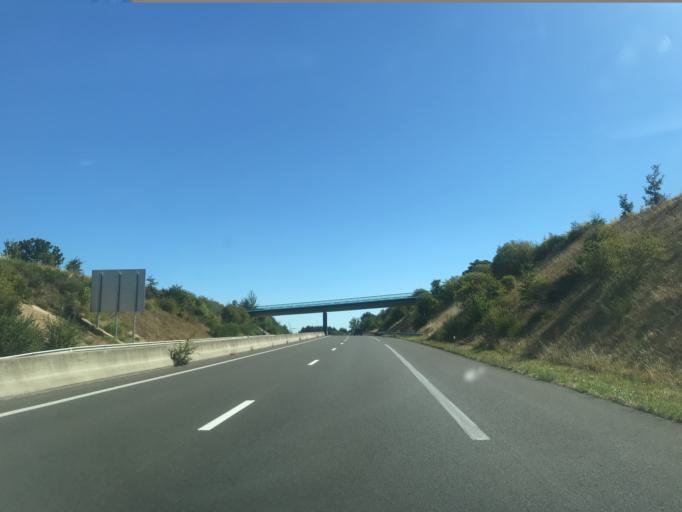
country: FR
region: Auvergne
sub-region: Departement de l'Allier
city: Huriel
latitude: 46.2962
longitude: 2.4311
